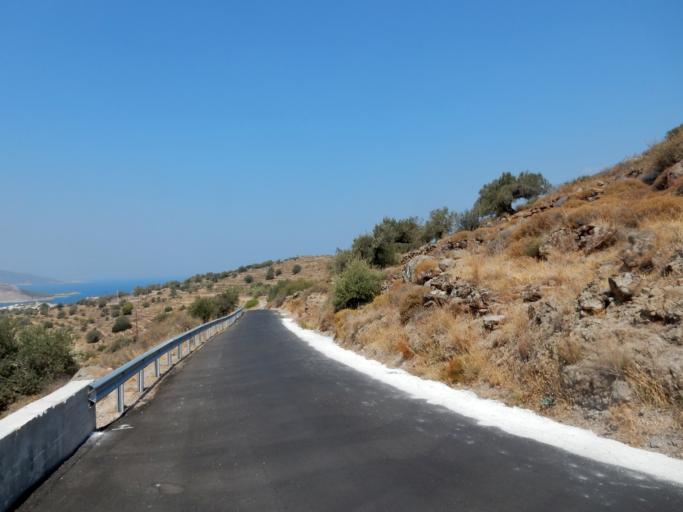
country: GR
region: Attica
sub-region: Nomos Piraios
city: Kypseli
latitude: 37.6898
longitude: 23.4771
